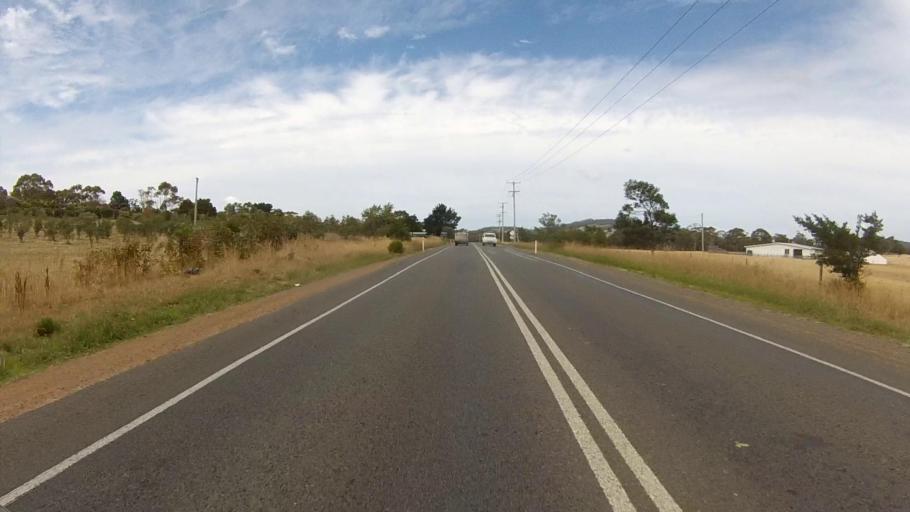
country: AU
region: Tasmania
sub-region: Clarence
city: Sandford
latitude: -42.9318
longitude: 147.4912
